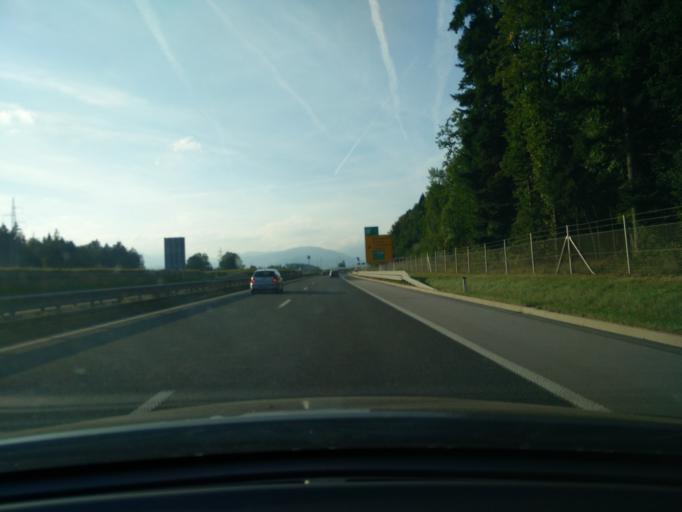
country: SI
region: Radovljica
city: Radovljica
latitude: 46.3349
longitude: 14.1976
